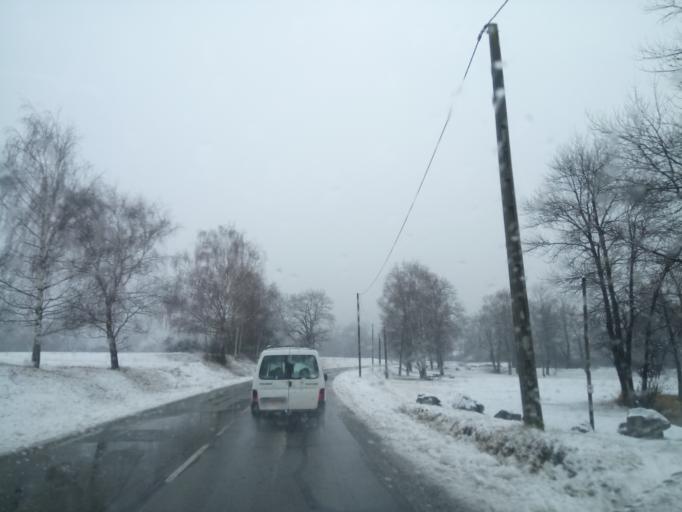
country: FR
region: Rhone-Alpes
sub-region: Departement de la Savoie
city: La Chambre
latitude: 45.3534
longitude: 6.2969
